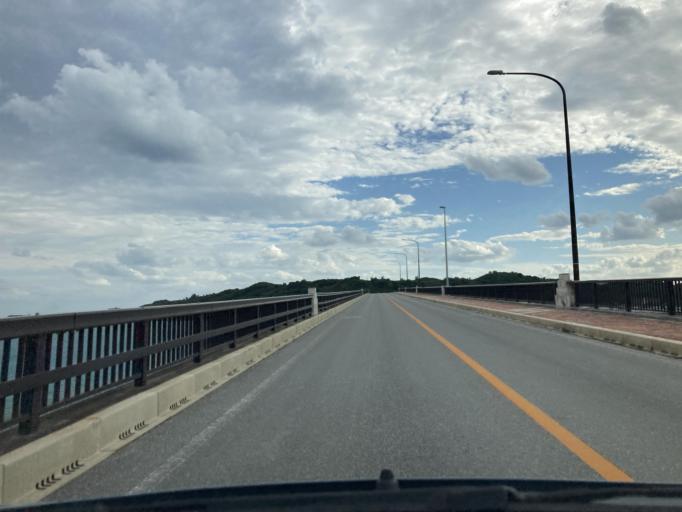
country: JP
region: Okinawa
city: Katsuren-haebaru
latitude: 26.3347
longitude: 127.9557
